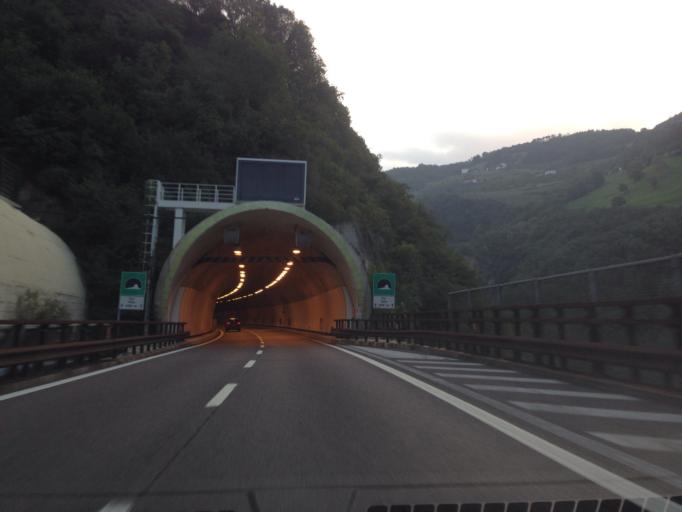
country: IT
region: Trentino-Alto Adige
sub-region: Bolzano
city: Fie Allo Sciliar
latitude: 46.5226
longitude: 11.4846
